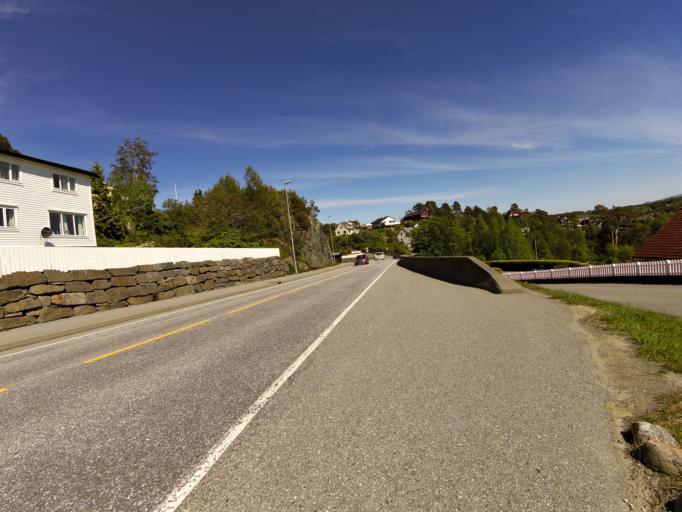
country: NO
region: Hordaland
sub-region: Stord
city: Sagvag
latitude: 59.7813
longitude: 5.3866
